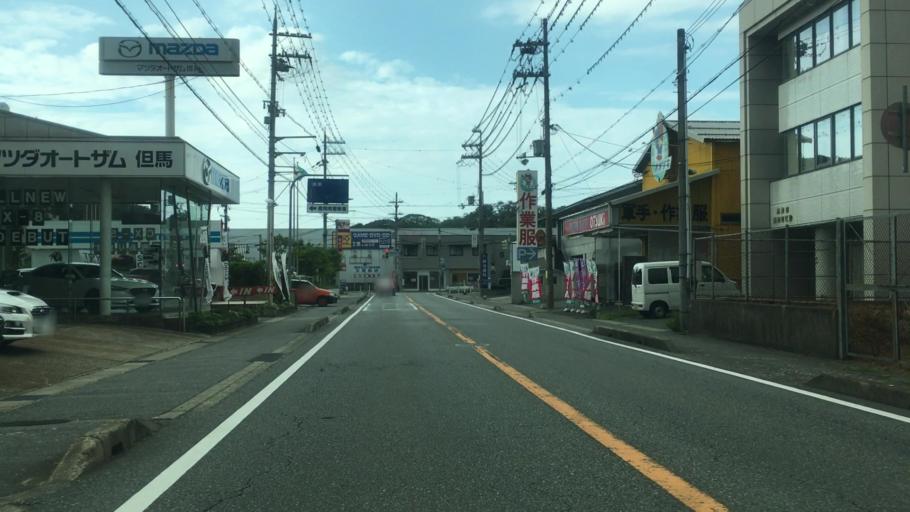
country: JP
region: Hyogo
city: Toyooka
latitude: 35.5337
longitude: 134.8198
